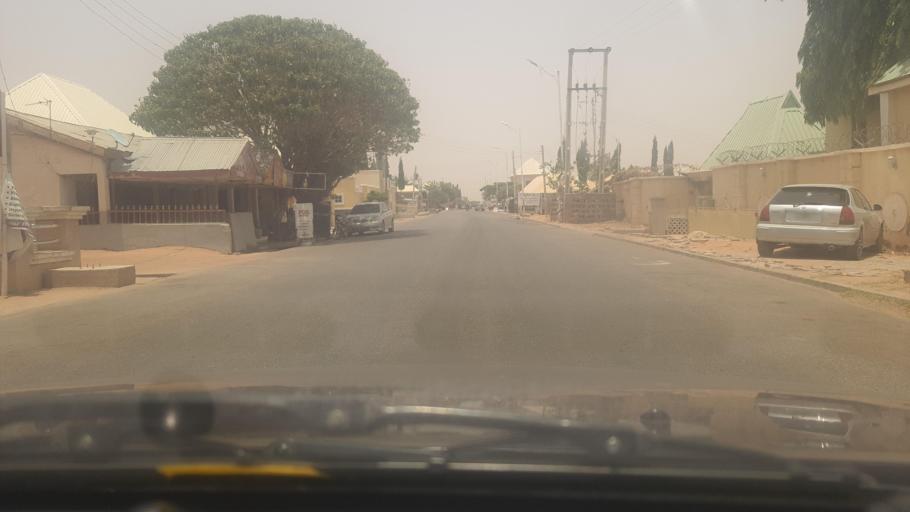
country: NG
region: Gombe
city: Gombe
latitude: 10.3030
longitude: 11.1473
